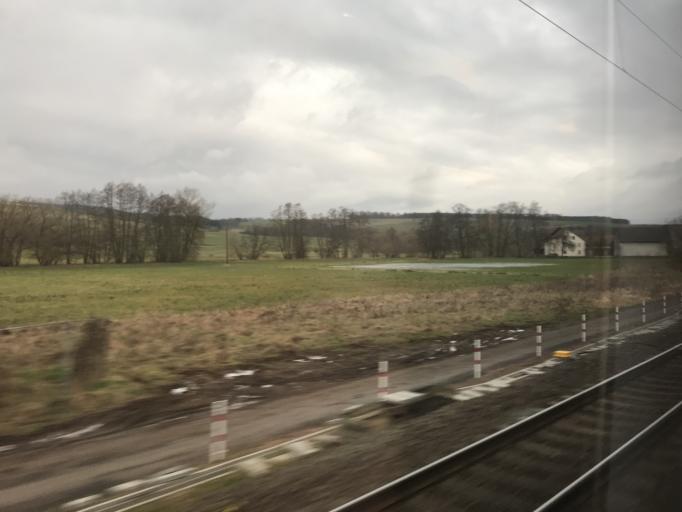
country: DE
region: Hesse
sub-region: Regierungsbezirk Kassel
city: Burghaun
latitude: 50.7669
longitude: 9.6910
